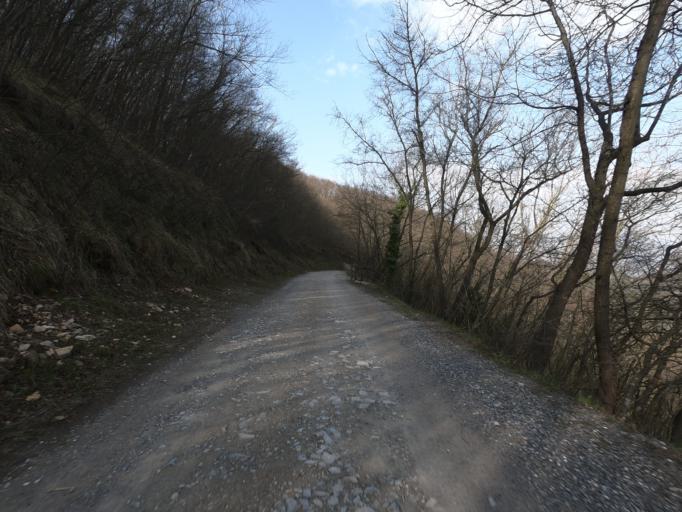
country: IT
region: Liguria
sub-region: Provincia di Savona
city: Balestrino
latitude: 44.1118
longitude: 8.1586
